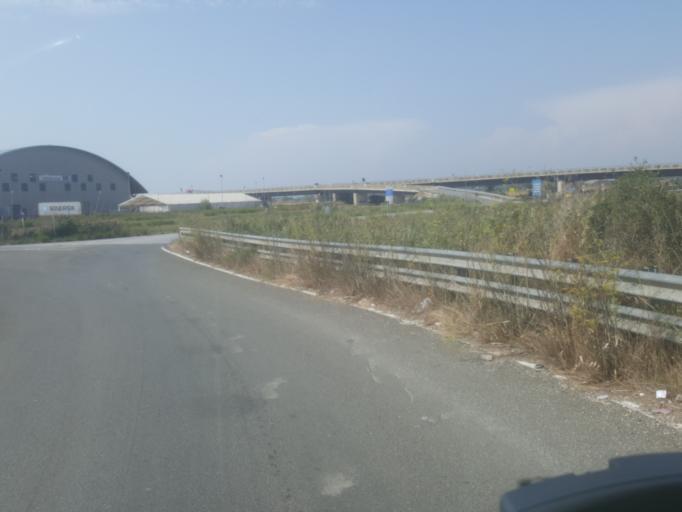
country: IT
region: Tuscany
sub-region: Provincia di Livorno
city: Guasticce
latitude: 43.6070
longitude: 10.4082
